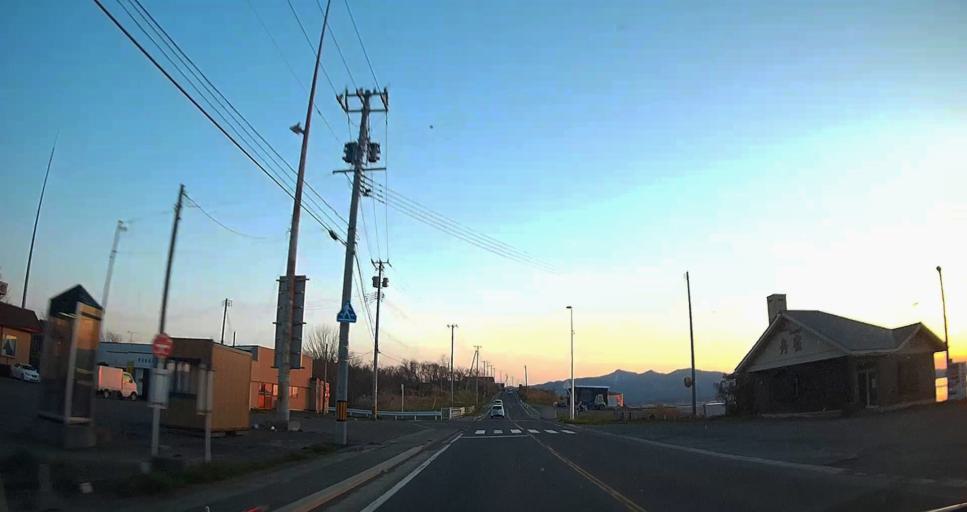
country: JP
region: Aomori
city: Misawa
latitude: 40.8804
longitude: 141.1514
